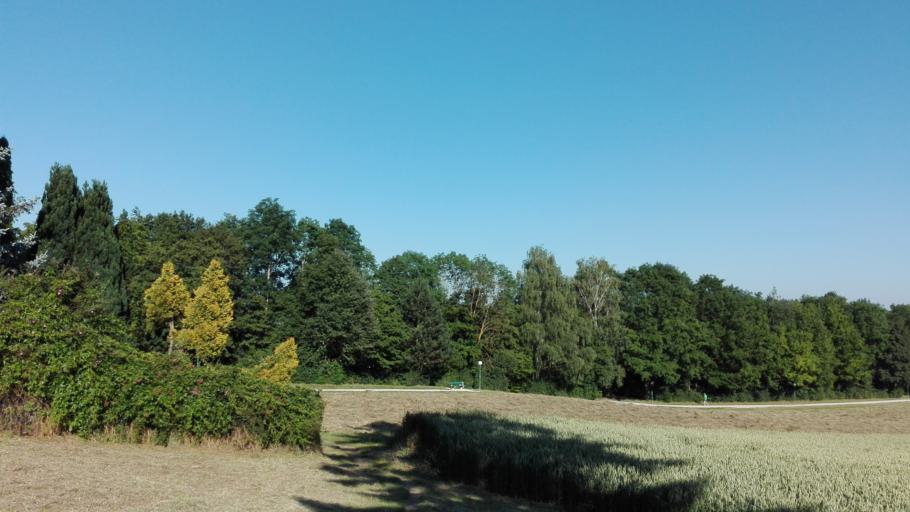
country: AT
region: Upper Austria
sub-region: Linz Stadt
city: Linz
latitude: 48.2692
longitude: 14.2998
